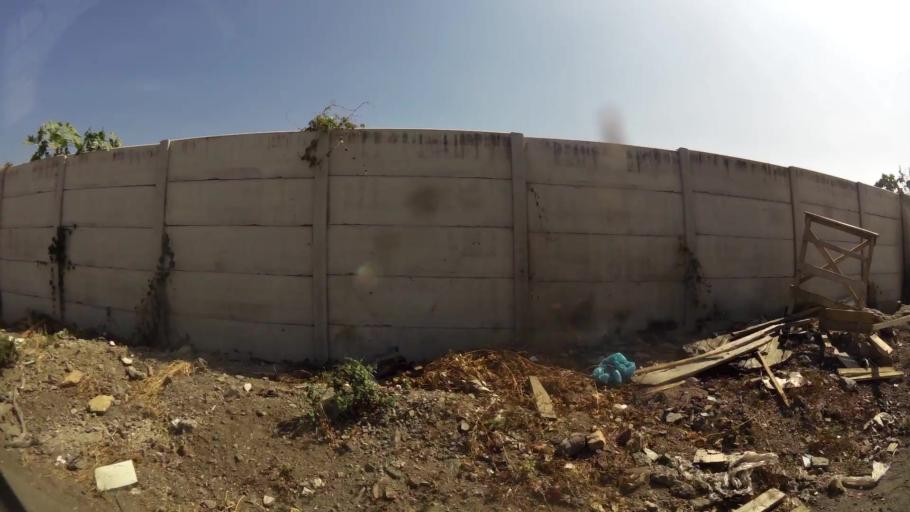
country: EC
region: Guayas
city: Guayaquil
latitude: -2.1879
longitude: -79.9130
